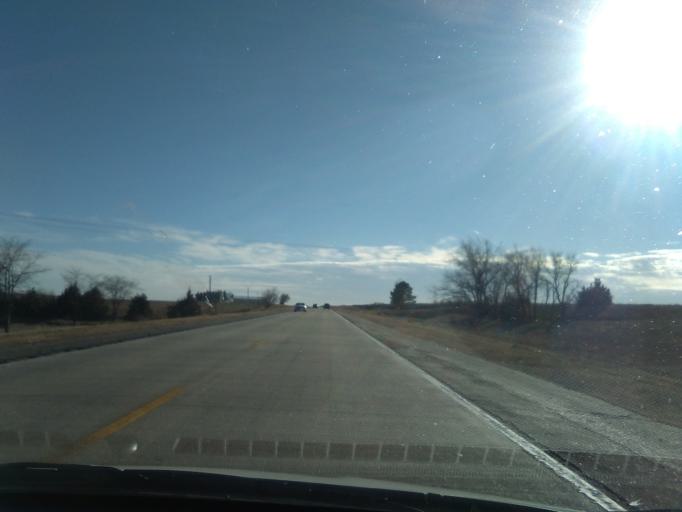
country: US
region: Nebraska
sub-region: Adams County
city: Hastings
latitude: 40.4245
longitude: -98.4392
